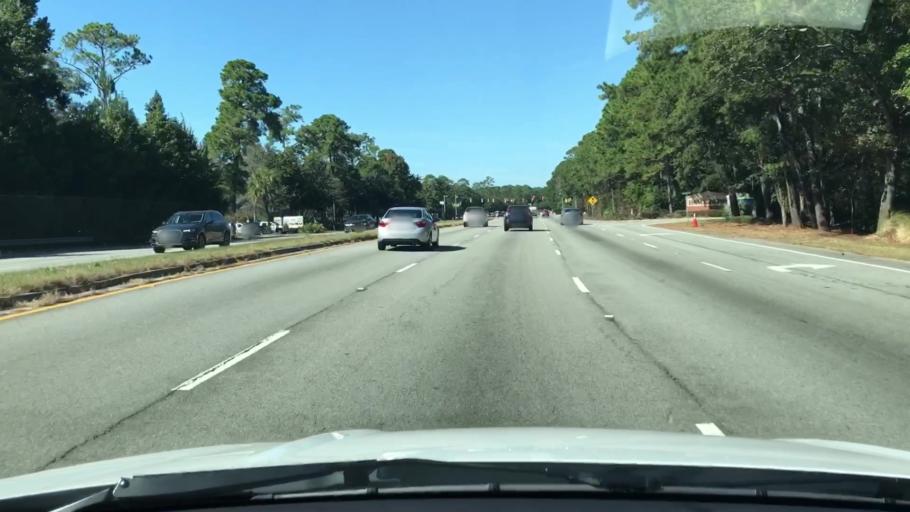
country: US
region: South Carolina
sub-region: Beaufort County
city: Bluffton
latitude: 32.2533
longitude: -80.8460
